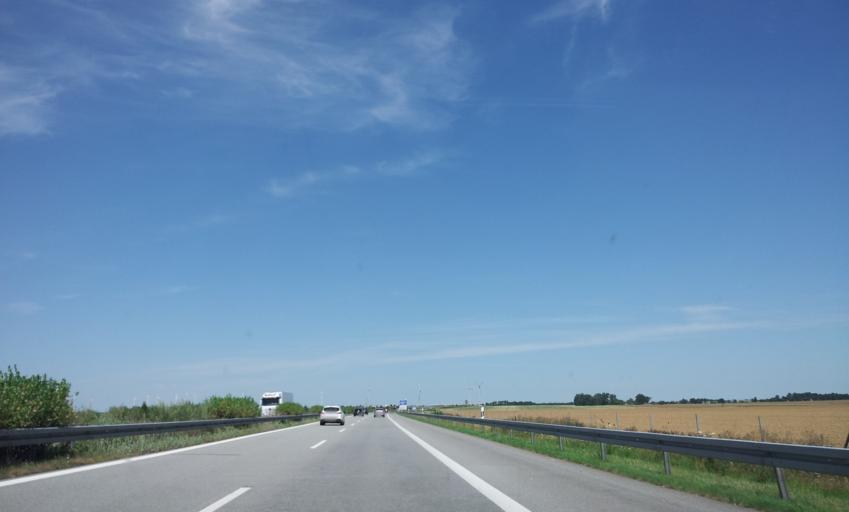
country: DE
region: Mecklenburg-Vorpommern
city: Jarmen
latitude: 53.8421
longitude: 13.3294
